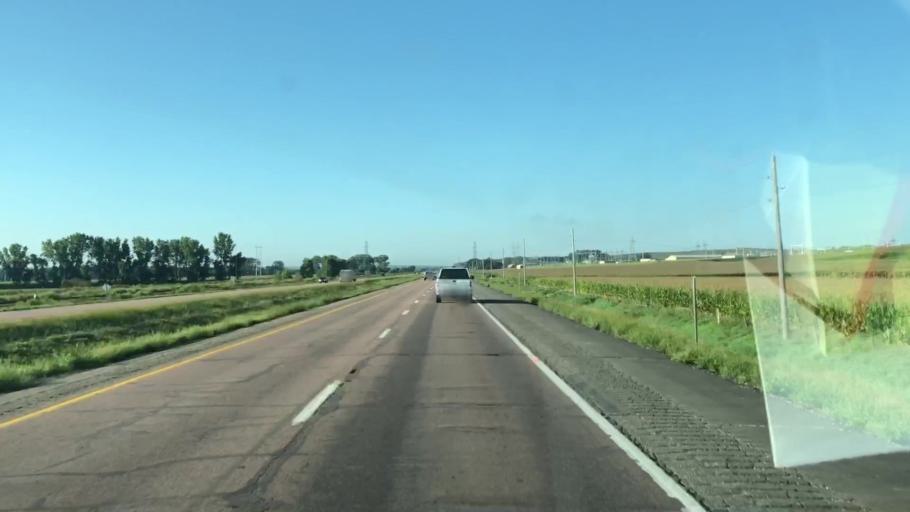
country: US
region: Iowa
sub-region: Woodbury County
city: Sioux City
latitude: 42.6104
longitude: -96.2973
